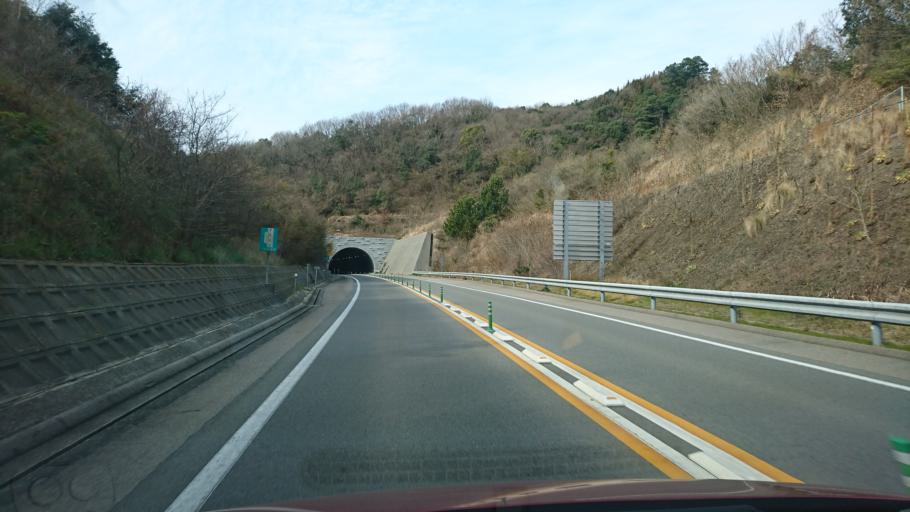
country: JP
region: Hiroshima
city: Innoshima
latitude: 34.1311
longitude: 133.0281
